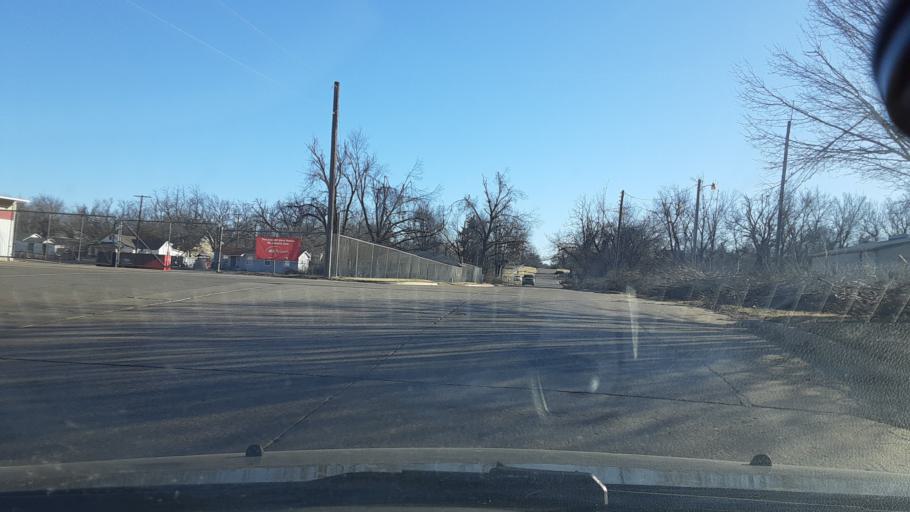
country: US
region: Oklahoma
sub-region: Logan County
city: Guthrie
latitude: 35.8728
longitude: -97.4251
